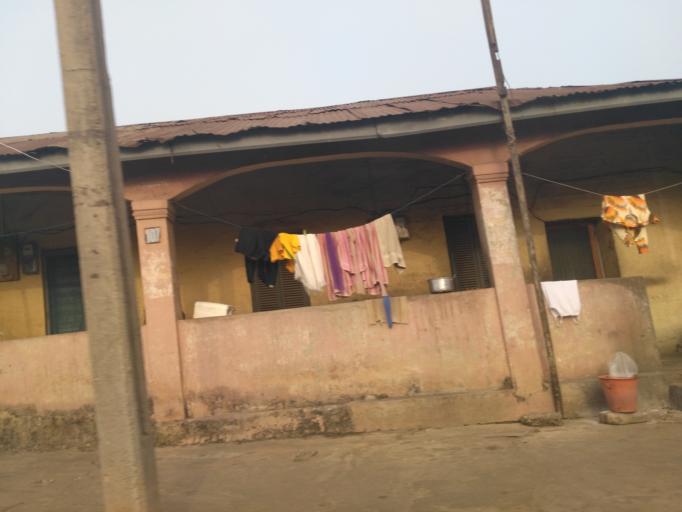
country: GH
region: Ashanti
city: Kumasi
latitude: 6.6871
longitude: -1.6136
